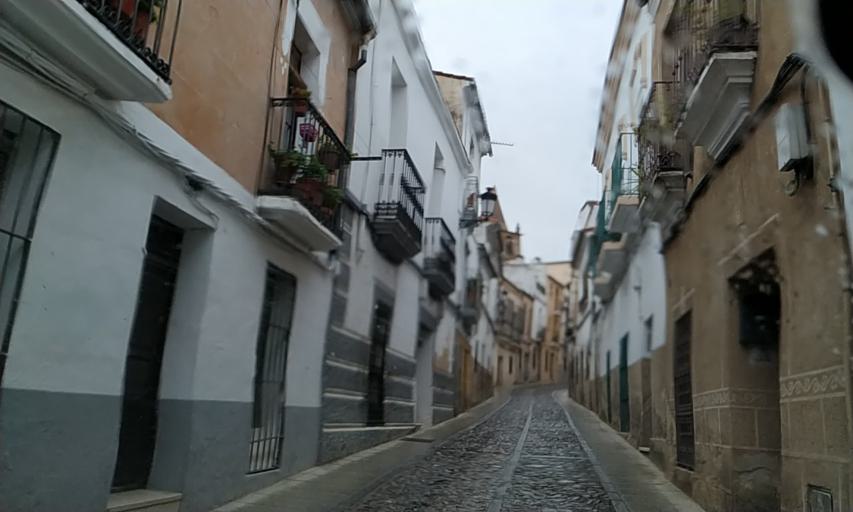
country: ES
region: Extremadura
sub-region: Provincia de Caceres
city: Caceres
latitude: 39.4773
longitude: -6.3693
